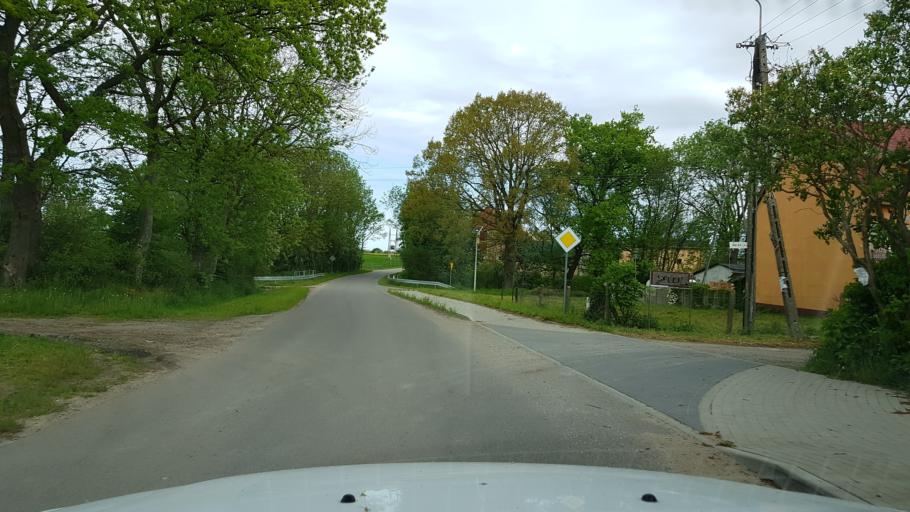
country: PL
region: West Pomeranian Voivodeship
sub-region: Powiat kolobrzeski
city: Ustronie Morskie
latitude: 54.2118
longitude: 15.8227
